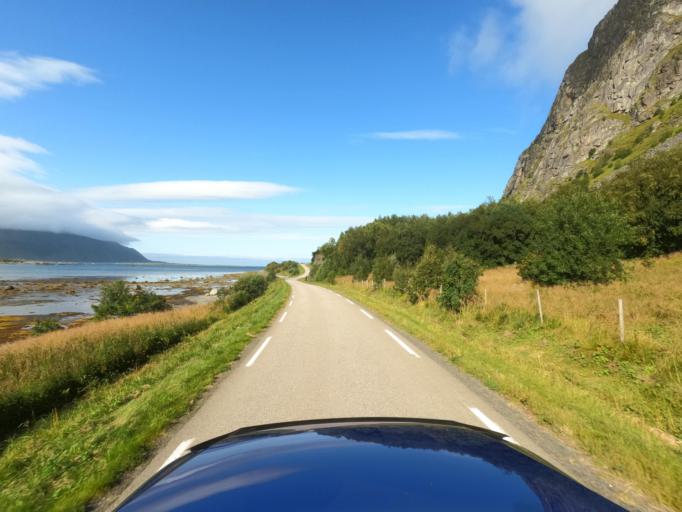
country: NO
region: Nordland
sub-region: Vestvagoy
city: Evjen
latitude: 68.3253
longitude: 14.1052
